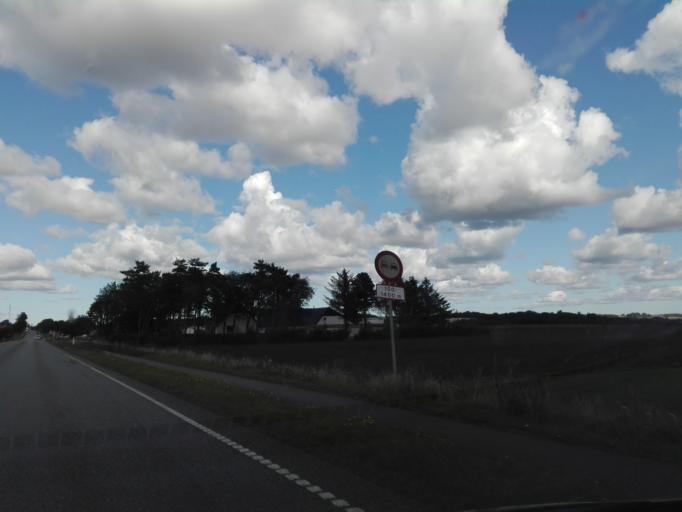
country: DK
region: North Denmark
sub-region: Mariagerfjord Kommune
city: Hobro
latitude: 56.6131
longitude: 9.8066
